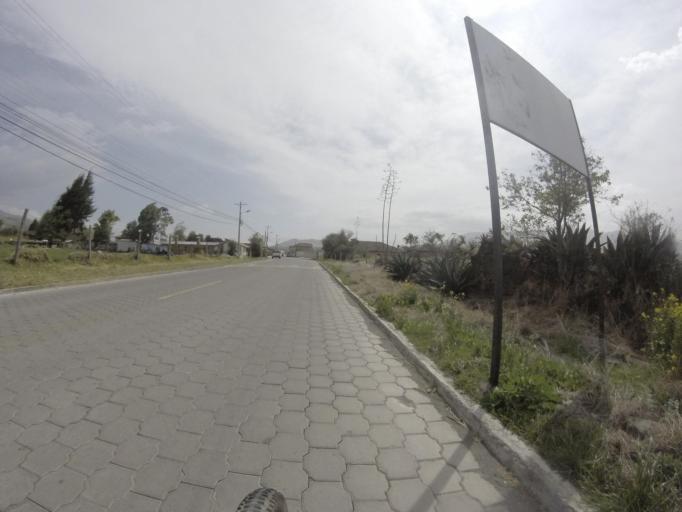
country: EC
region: Pichincha
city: Cayambe
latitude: 0.1404
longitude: -78.0758
